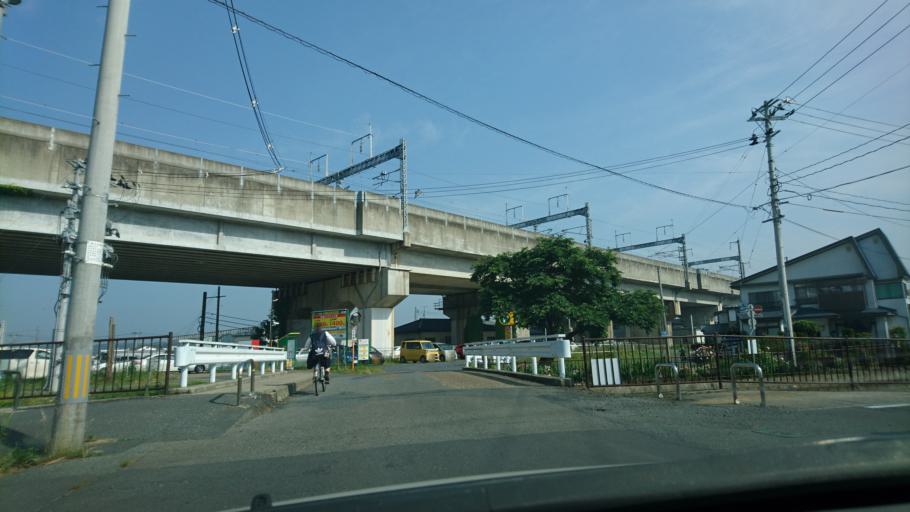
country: JP
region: Iwate
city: Ichinoseki
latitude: 38.9283
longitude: 141.1406
